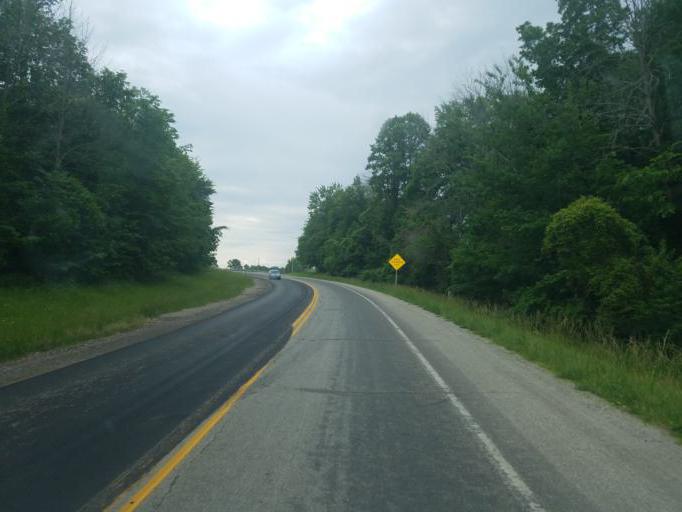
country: US
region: Ohio
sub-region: Knox County
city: Fredericktown
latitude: 40.5398
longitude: -82.6638
